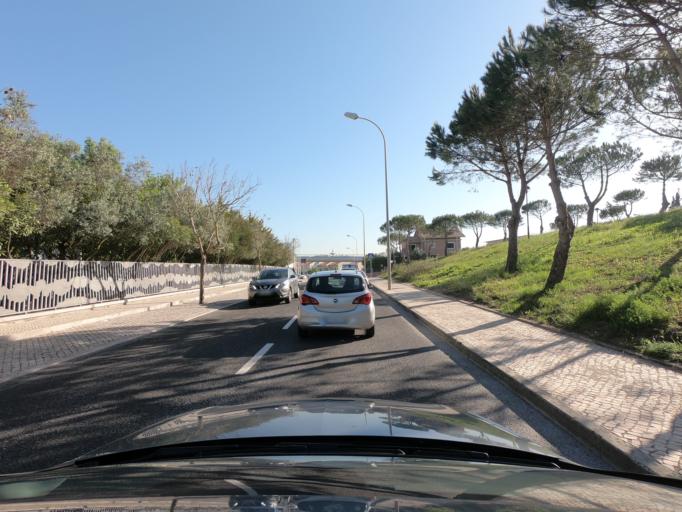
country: PT
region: Lisbon
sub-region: Oeiras
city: Paco de Arcos
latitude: 38.7025
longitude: -9.3012
